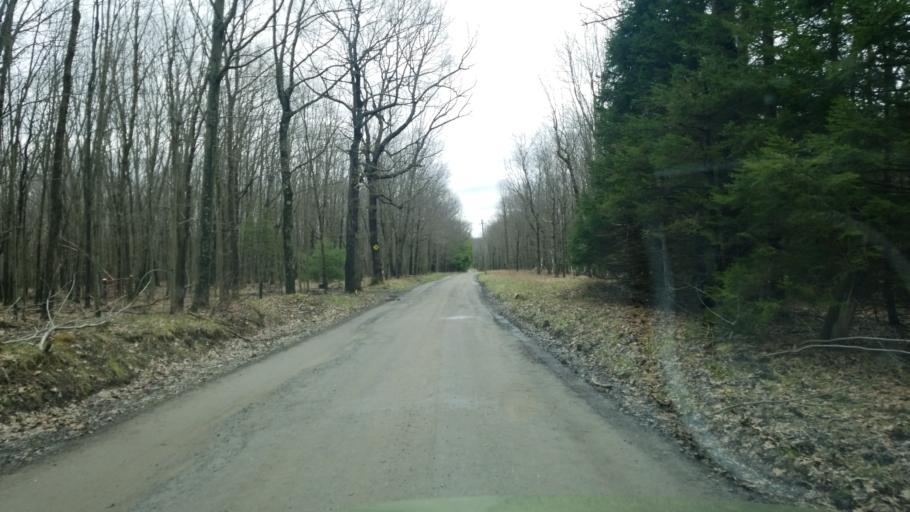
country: US
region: Pennsylvania
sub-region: Clearfield County
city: Shiloh
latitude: 41.1801
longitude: -78.3337
